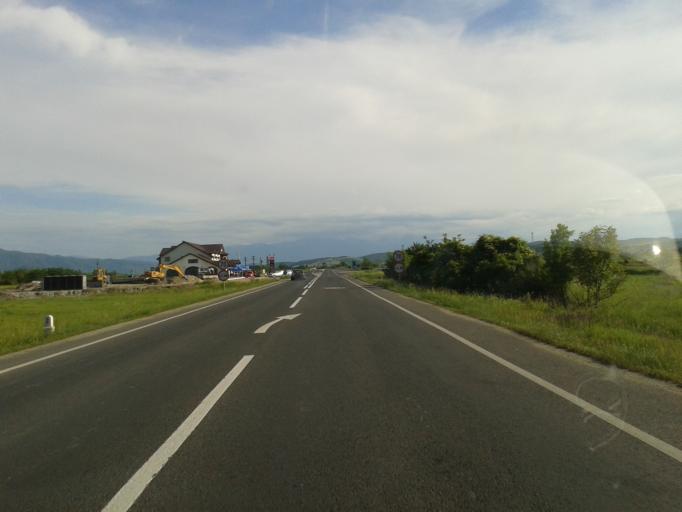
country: RO
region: Hunedoara
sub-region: Comuna Calan
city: Calan
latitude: 45.7274
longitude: 22.9956
